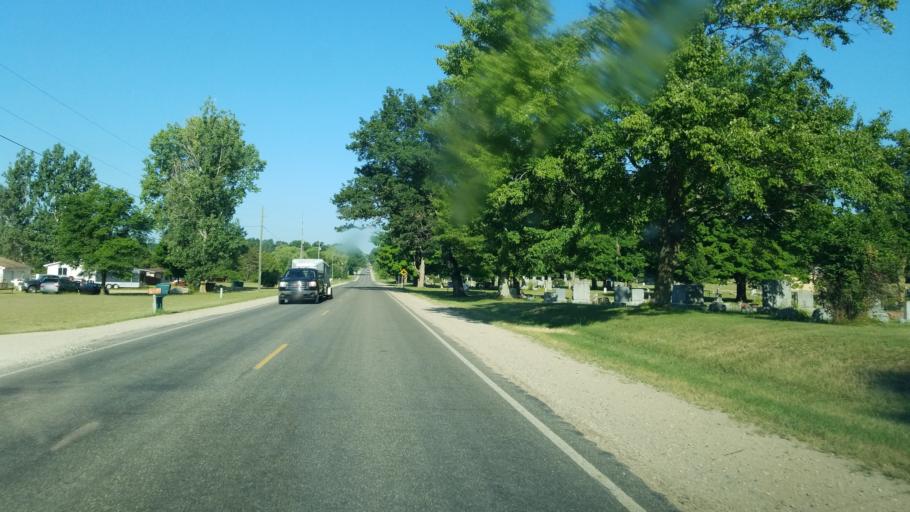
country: US
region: Michigan
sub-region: Montcalm County
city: Howard City
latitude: 43.4899
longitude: -85.4592
